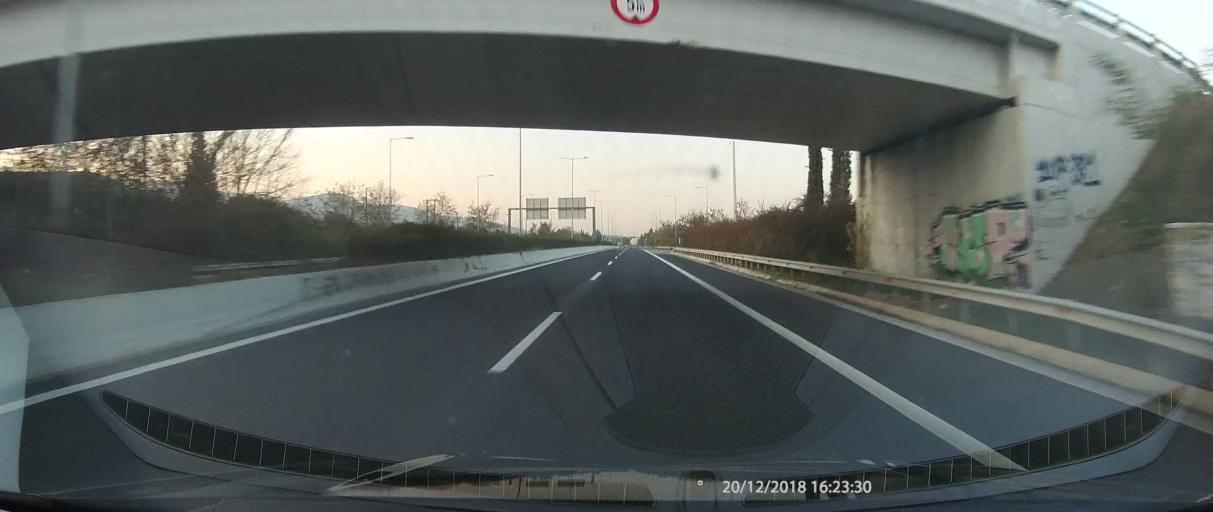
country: GR
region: Thessaly
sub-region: Nomos Magnisias
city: Sourpi
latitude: 39.0916
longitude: 22.8725
